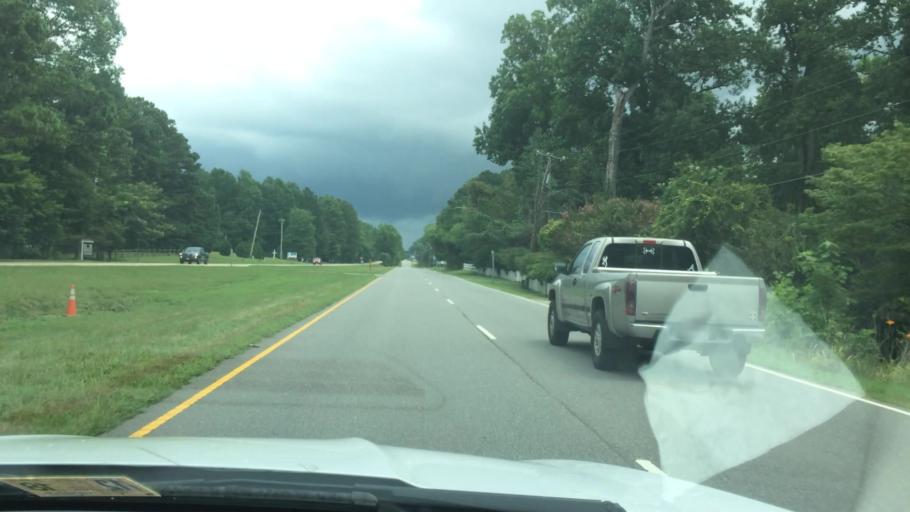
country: US
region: Virginia
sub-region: King William County
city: West Point
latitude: 37.4039
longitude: -76.8355
